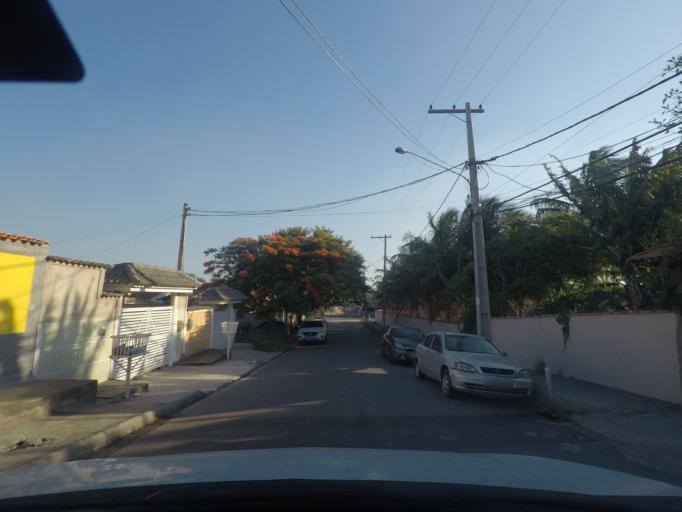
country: BR
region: Rio de Janeiro
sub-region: Marica
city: Marica
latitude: -22.9695
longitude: -42.9360
